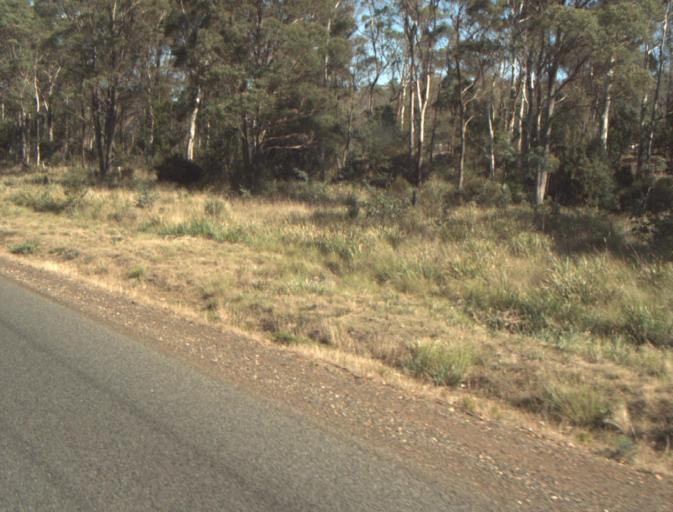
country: AU
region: Tasmania
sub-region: Launceston
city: Mayfield
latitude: -41.3242
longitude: 147.1373
